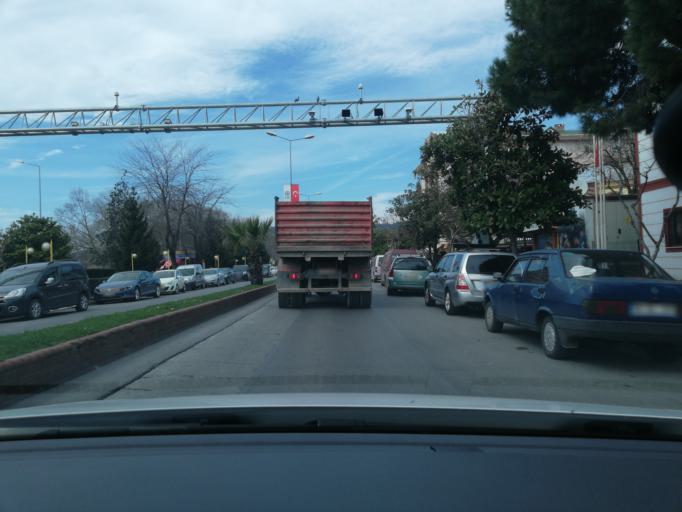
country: TR
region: Zonguldak
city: Eregli
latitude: 41.2830
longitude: 31.4148
